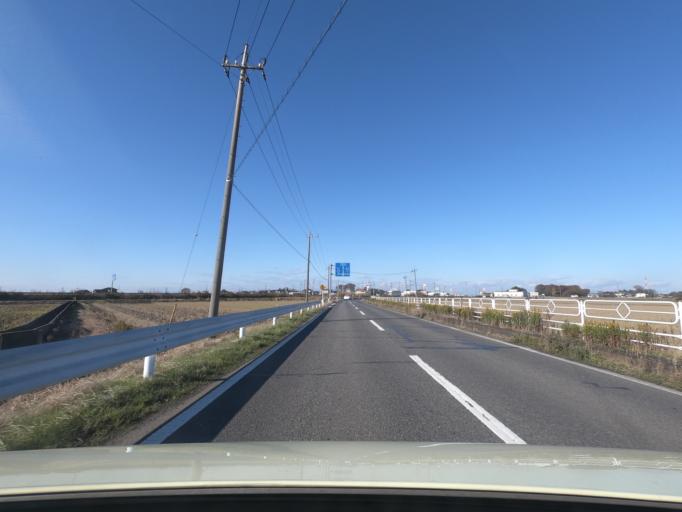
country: JP
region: Ibaraki
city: Ishige
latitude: 36.1575
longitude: 139.9965
